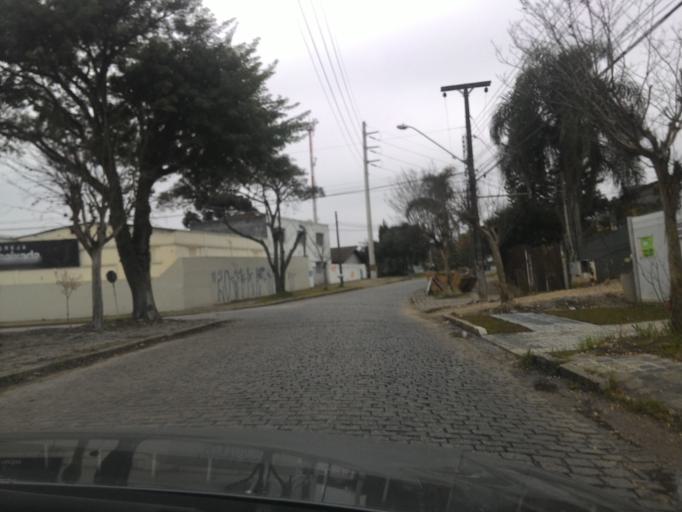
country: BR
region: Parana
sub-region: Curitiba
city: Curitiba
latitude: -25.4608
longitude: -49.2468
